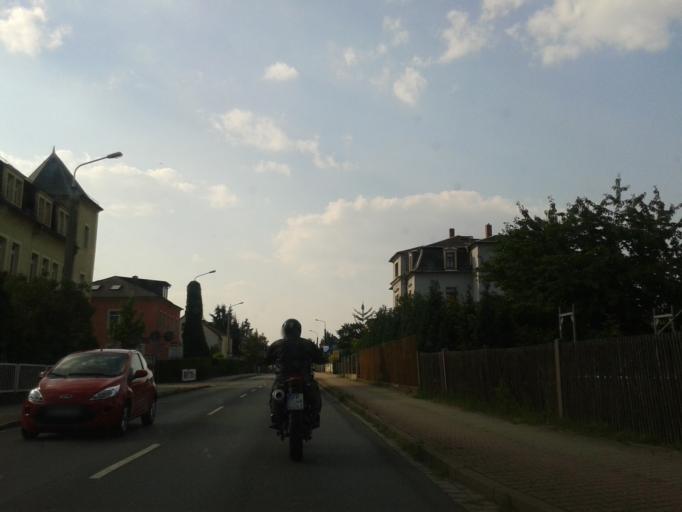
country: DE
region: Saxony
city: Radebeul
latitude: 51.0759
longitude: 13.6658
